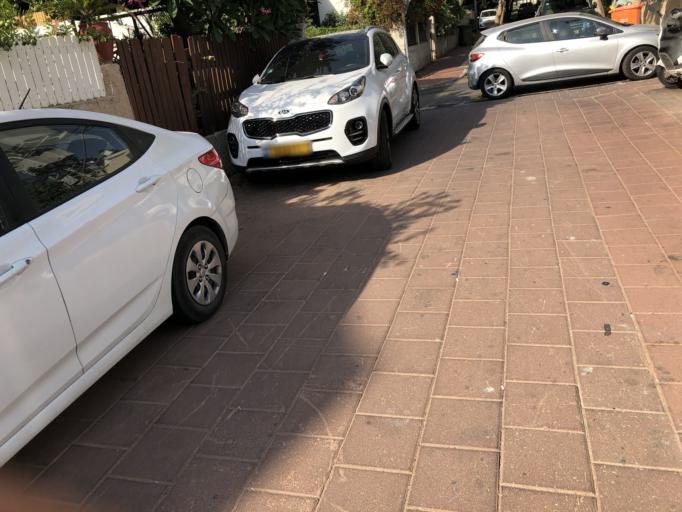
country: IL
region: Tel Aviv
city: Giv`atayim
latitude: 32.0677
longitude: 34.8191
